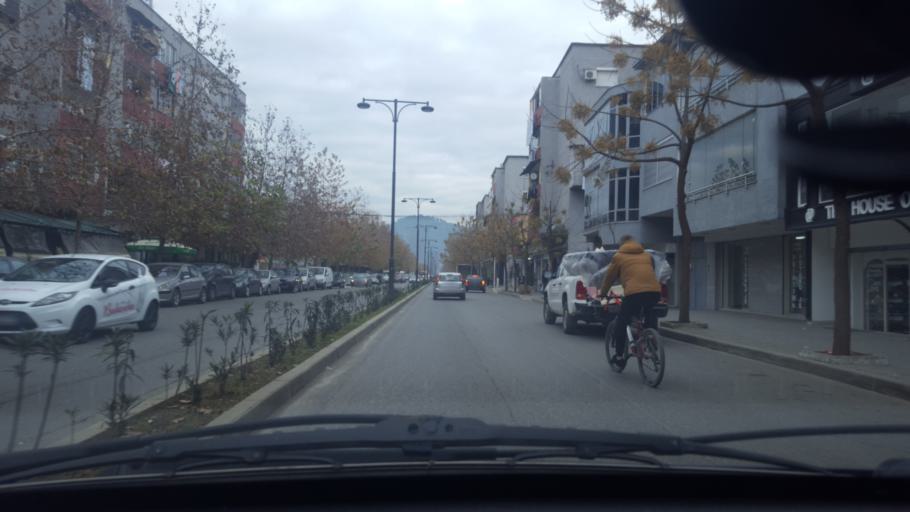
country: AL
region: Elbasan
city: Elbasan
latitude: 41.1125
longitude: 20.0856
